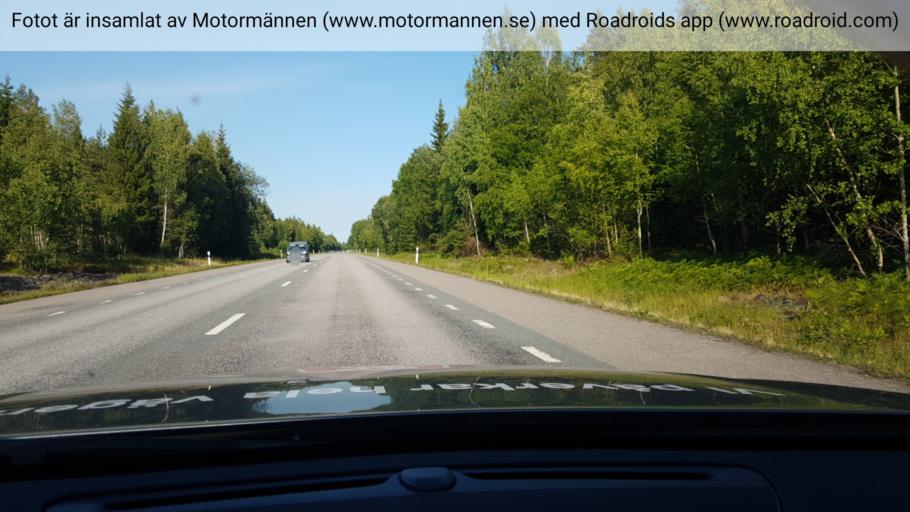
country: SE
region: Uppsala
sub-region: Osthammars Kommun
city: Gimo
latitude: 60.1643
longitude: 18.1139
